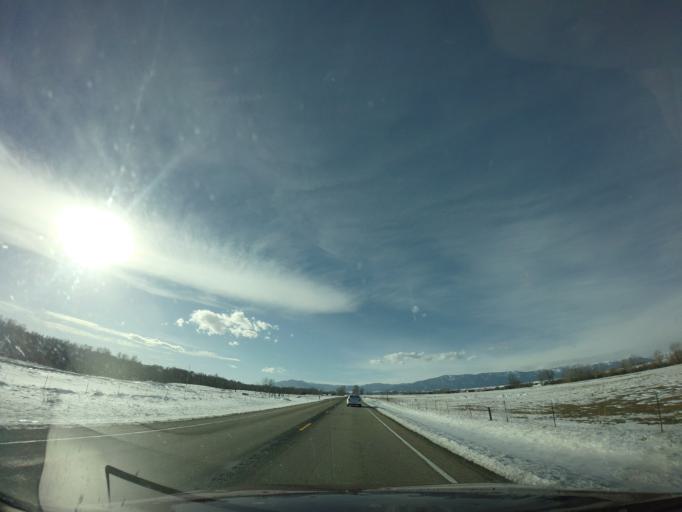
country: US
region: Montana
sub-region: Carbon County
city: Red Lodge
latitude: 45.3077
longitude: -109.1992
